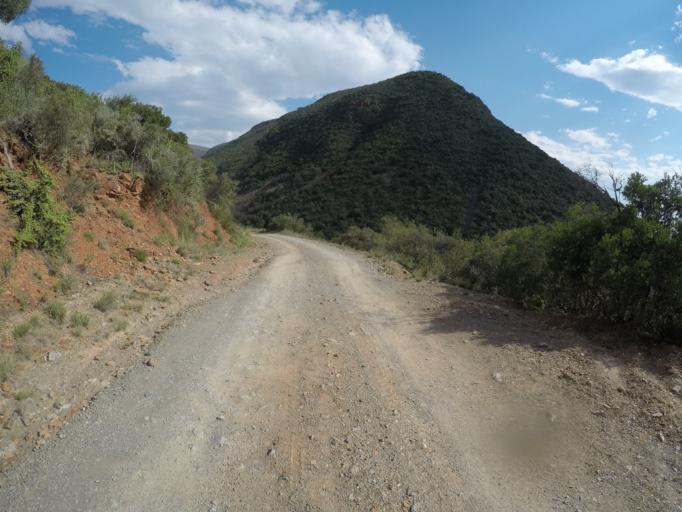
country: ZA
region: Eastern Cape
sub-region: Cacadu District Municipality
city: Kareedouw
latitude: -33.6491
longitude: 24.3371
